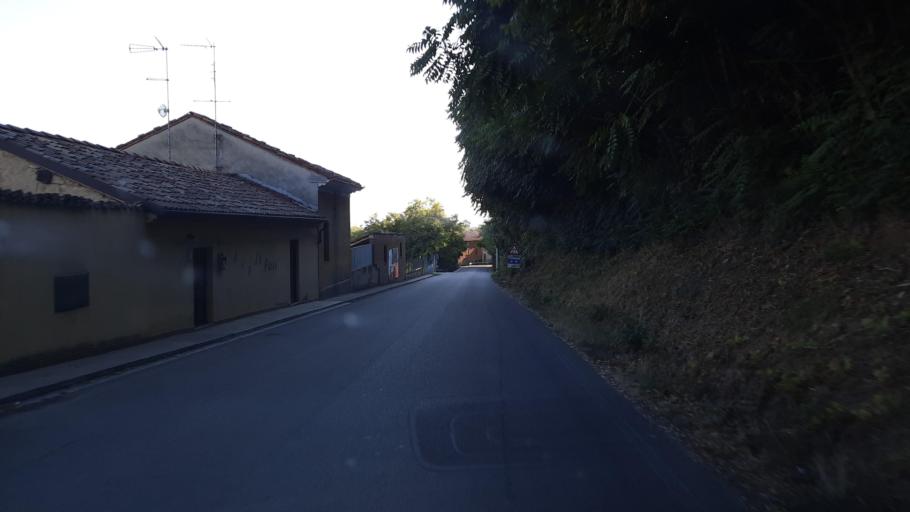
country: IT
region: Piedmont
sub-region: Provincia di Alessandria
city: Vignale Monferrato
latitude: 45.0095
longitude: 8.3965
